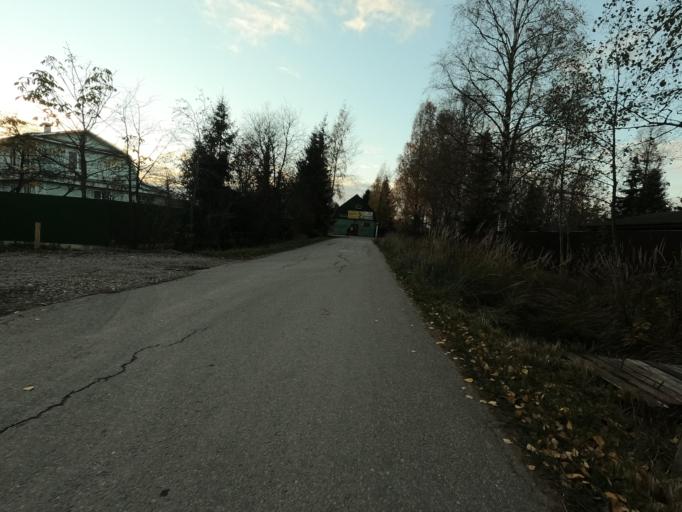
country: RU
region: Leningrad
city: Mga
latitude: 59.7769
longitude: 31.2067
